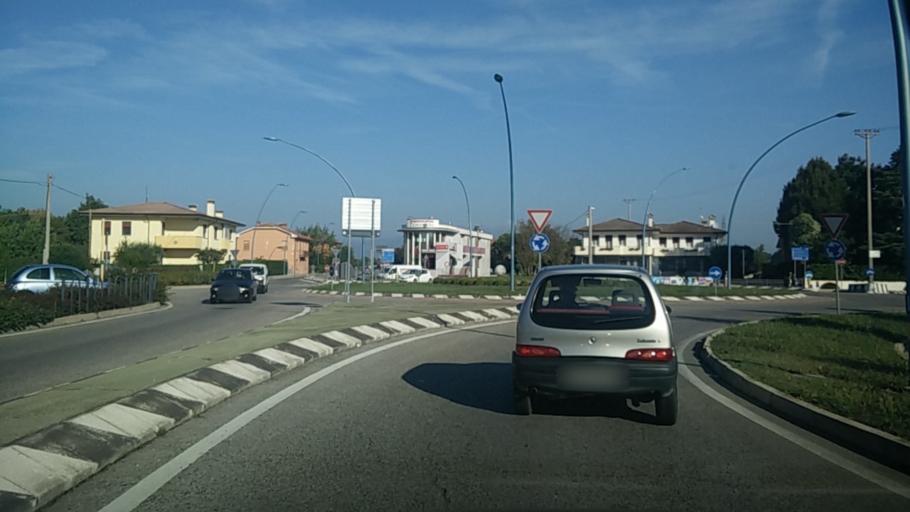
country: IT
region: Veneto
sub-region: Provincia di Treviso
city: Resana
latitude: 45.6395
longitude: 11.9531
